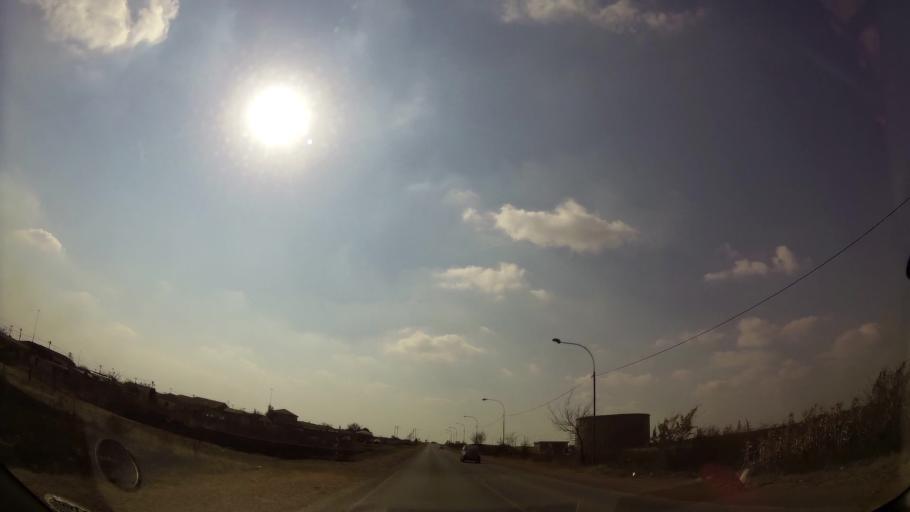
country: ZA
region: Gauteng
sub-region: Ekurhuleni Metropolitan Municipality
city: Springs
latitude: -26.1281
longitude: 28.4880
